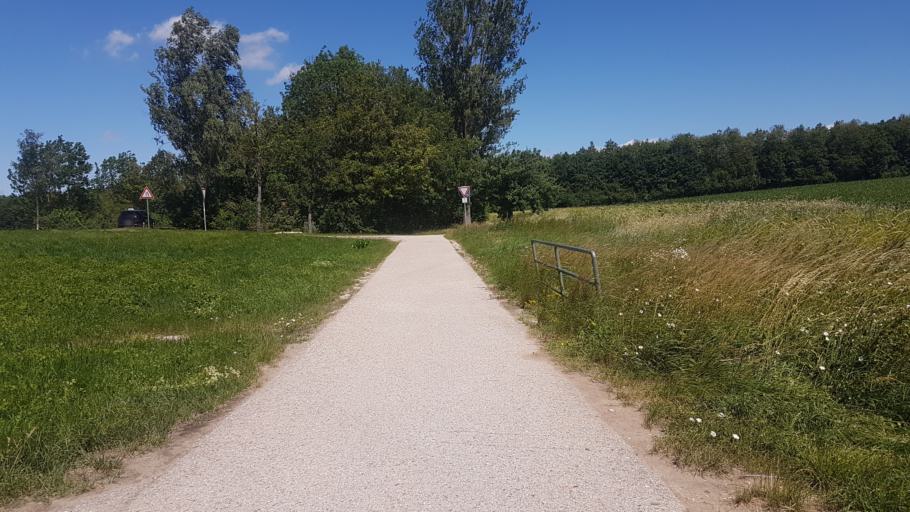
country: DE
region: Bavaria
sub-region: Regierungsbezirk Mittelfranken
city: Herrieden
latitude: 49.2471
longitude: 10.4671
